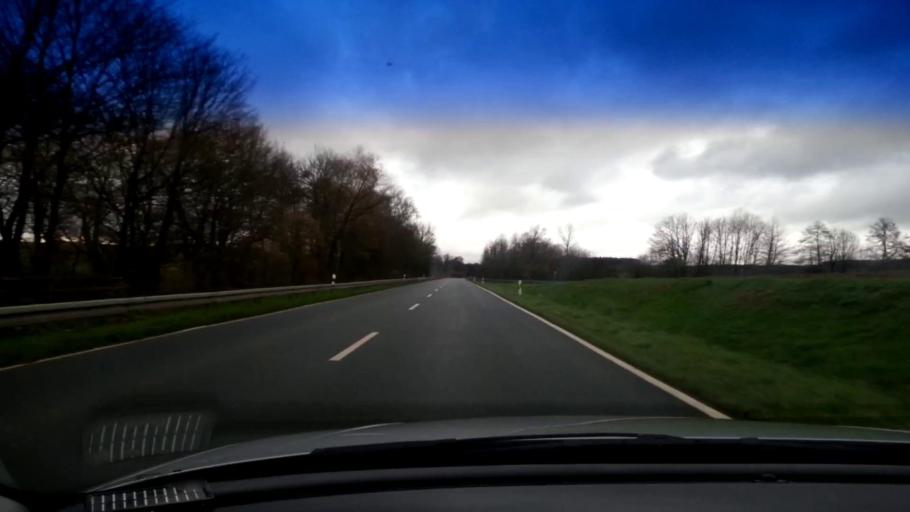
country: DE
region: Bavaria
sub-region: Upper Franconia
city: Ebensfeld
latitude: 50.0414
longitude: 10.9986
